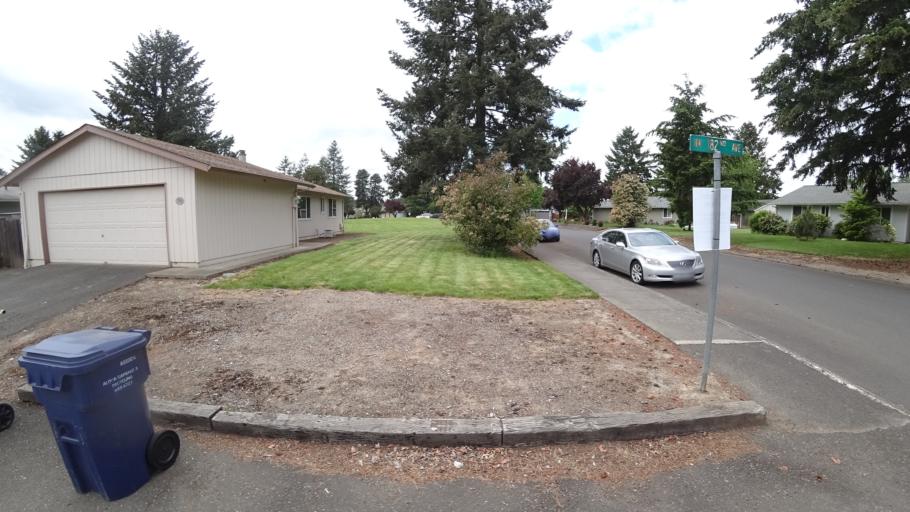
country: US
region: Oregon
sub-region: Washington County
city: Aloha
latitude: 45.5221
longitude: -122.8646
